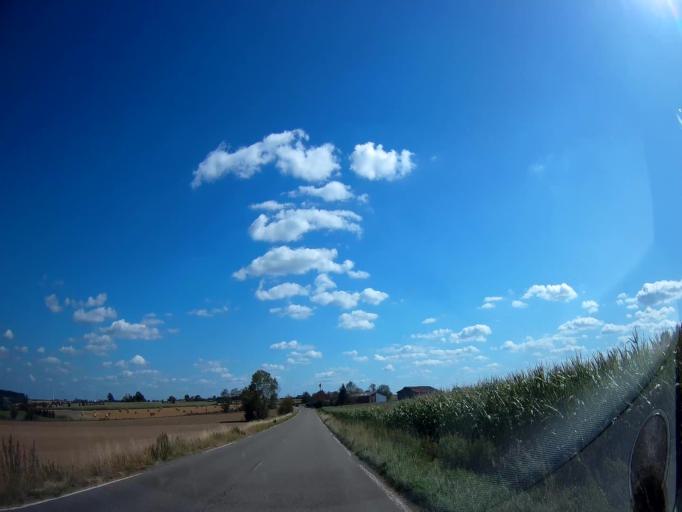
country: FR
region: Champagne-Ardenne
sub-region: Departement des Ardennes
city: Fromelennes
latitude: 50.1759
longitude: 4.8680
